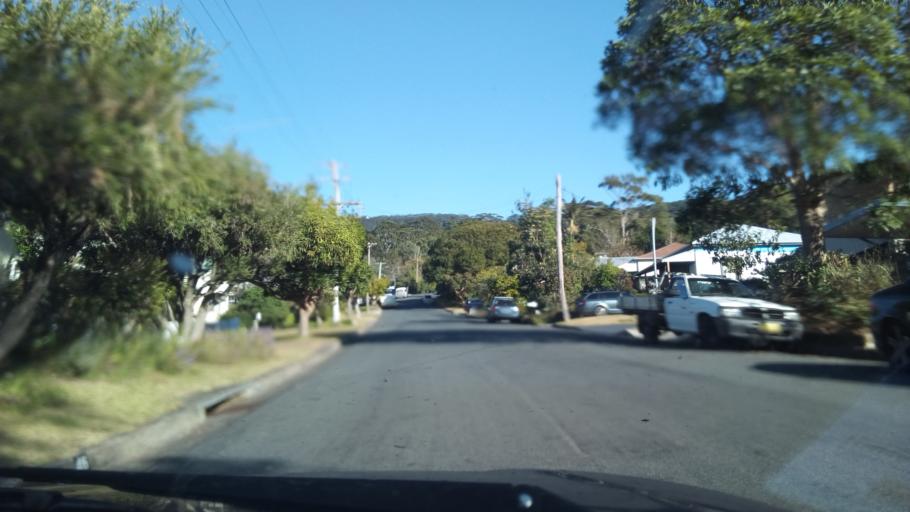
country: AU
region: New South Wales
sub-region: Wollongong
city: Bulli
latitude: -34.3177
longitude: 150.9120
